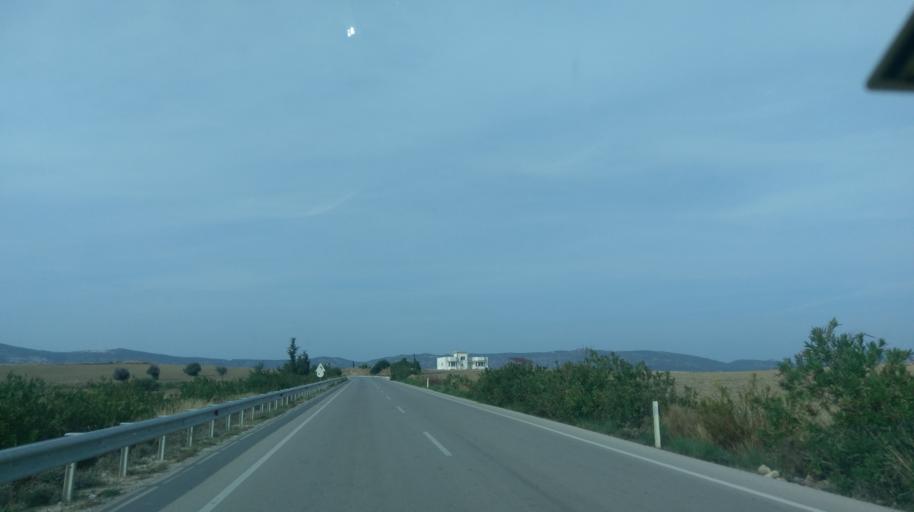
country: CY
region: Ammochostos
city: Leonarisso
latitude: 35.3890
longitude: 34.0101
